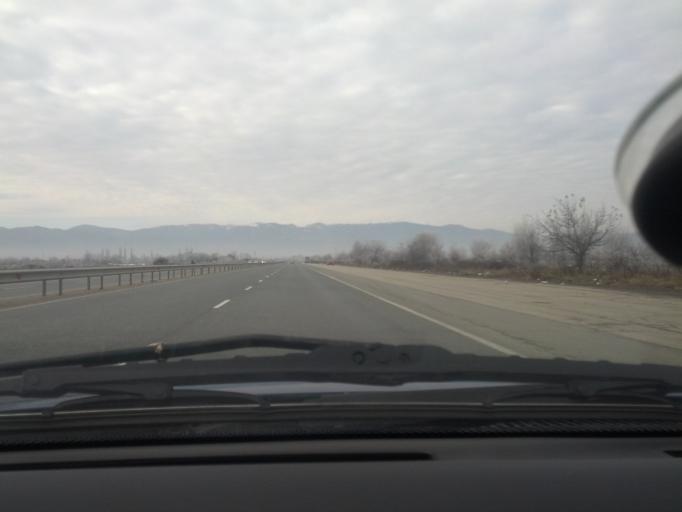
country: BG
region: Sofiya
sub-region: Obshtina Botevgrad
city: Botevgrad
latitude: 42.9234
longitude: 23.7972
